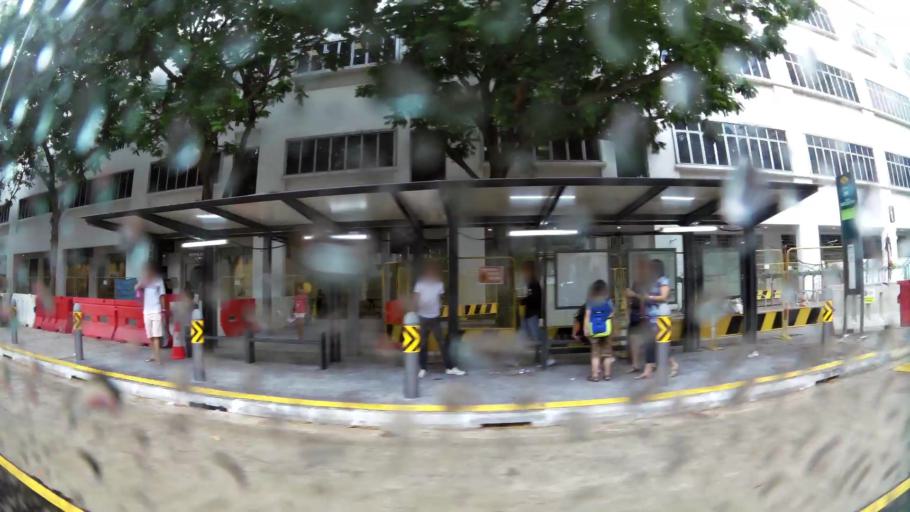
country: SG
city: Singapore
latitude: 1.2998
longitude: 103.8511
